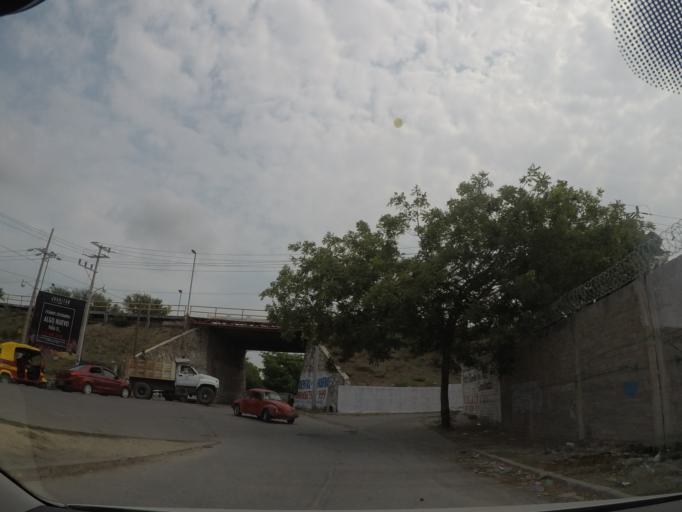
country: MX
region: Oaxaca
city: Juchitan de Zaragoza
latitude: 16.4465
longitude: -95.0215
